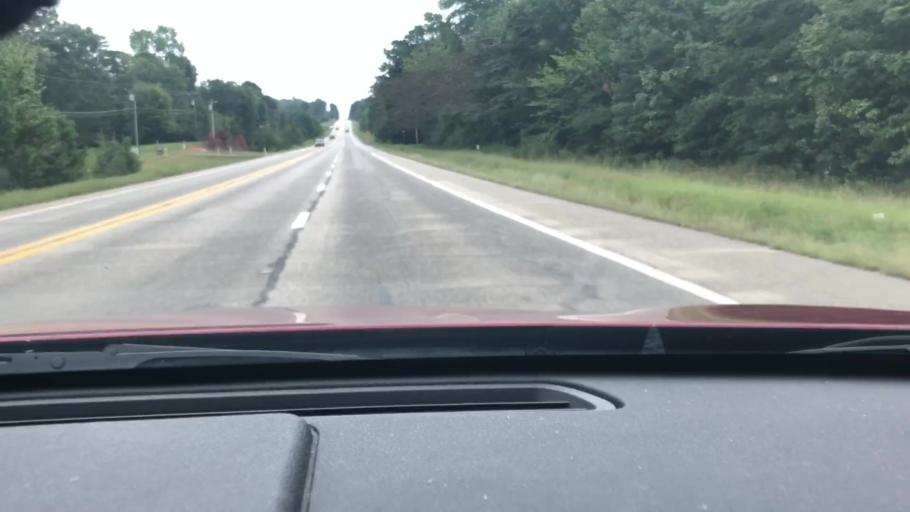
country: US
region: Arkansas
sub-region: Miller County
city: Texarkana
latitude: 33.4295
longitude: -93.9504
